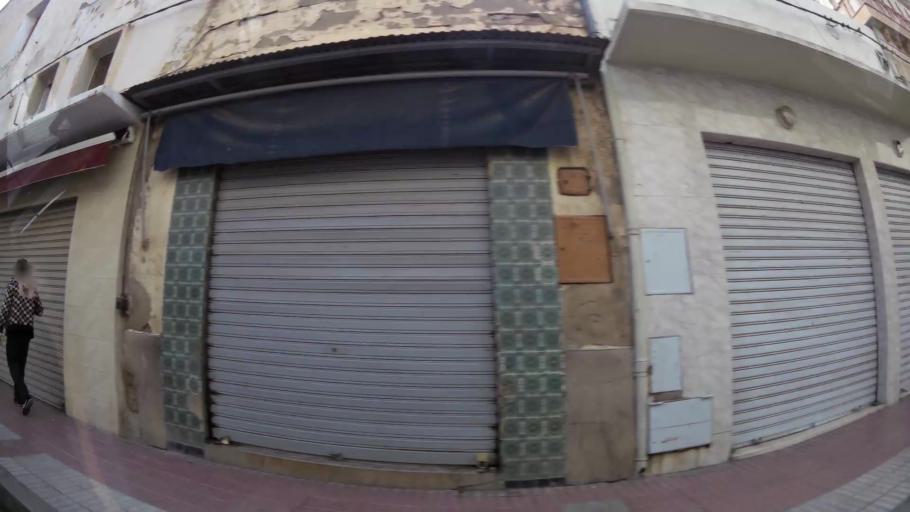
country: MA
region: Oriental
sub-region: Oujda-Angad
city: Oujda
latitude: 34.6818
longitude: -1.9150
